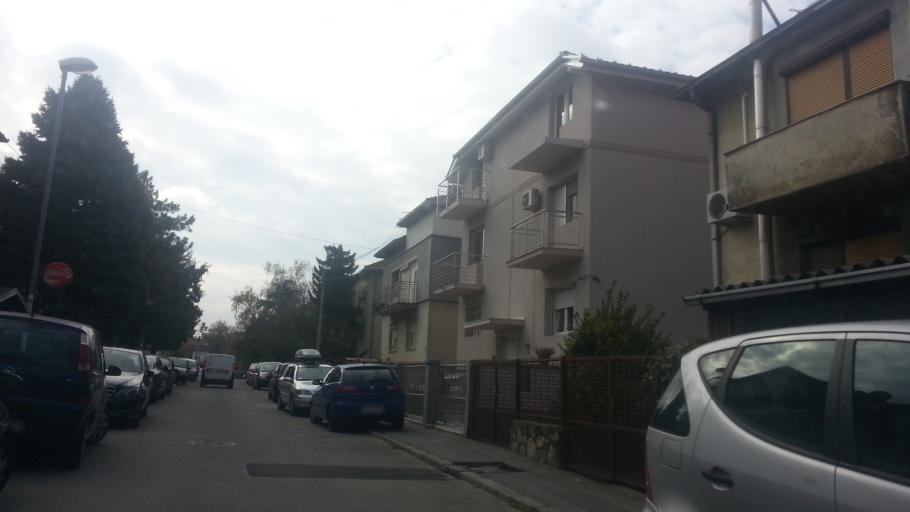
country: RS
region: Central Serbia
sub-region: Belgrade
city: Zemun
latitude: 44.8588
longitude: 20.3705
